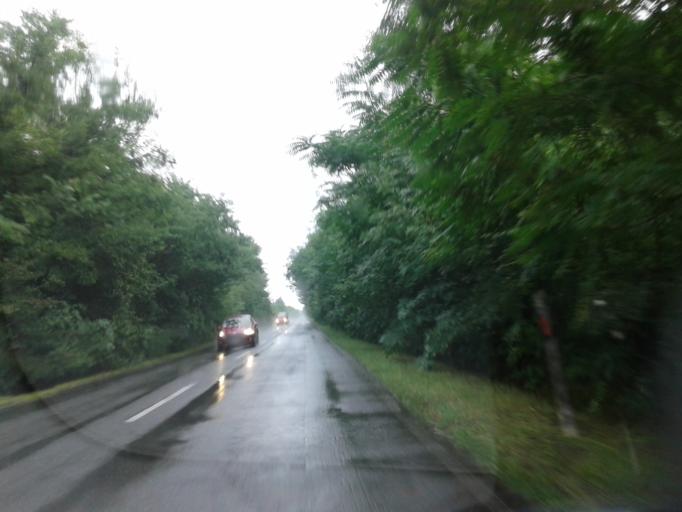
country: HU
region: Csongrad
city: Asotthalom
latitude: 46.2214
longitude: 19.7708
